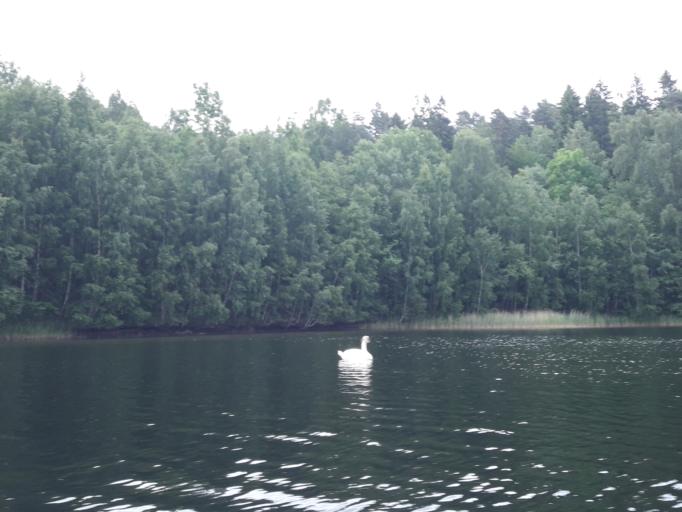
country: NO
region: Akershus
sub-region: Frogn
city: Drobak
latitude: 59.6663
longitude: 10.5855
